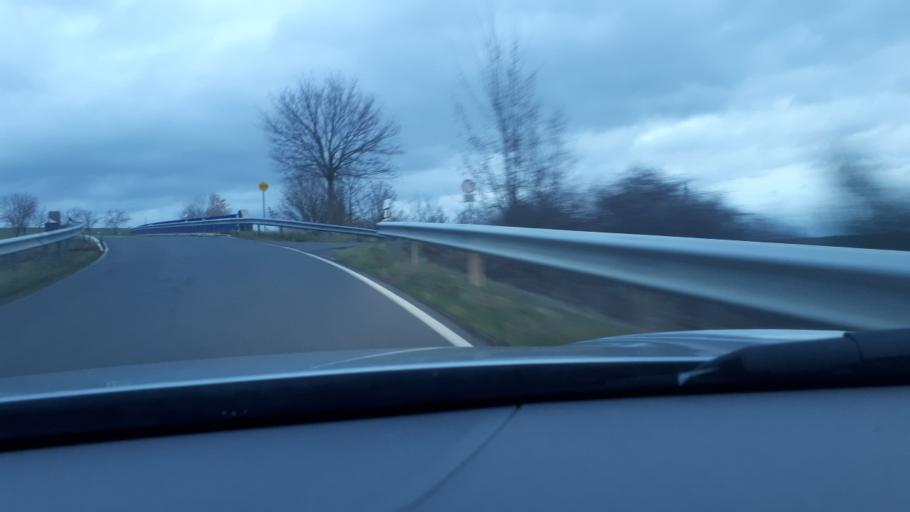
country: DE
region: Rheinland-Pfalz
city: Mayen
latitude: 50.3118
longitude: 7.2255
